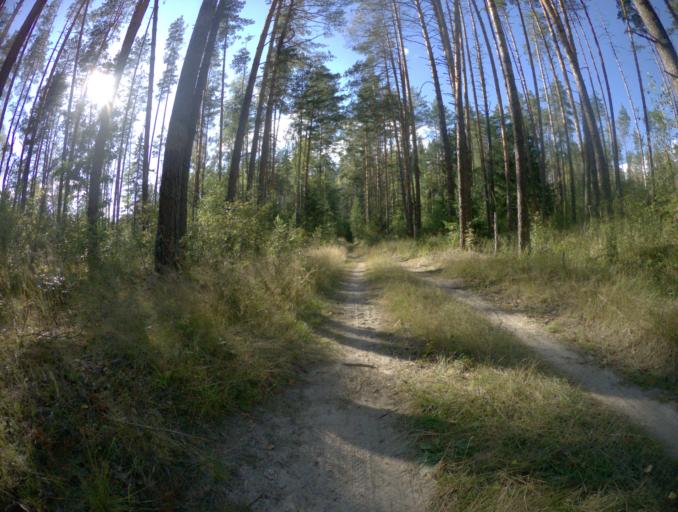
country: RU
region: Vladimir
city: Krasnaya Gorbatka
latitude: 55.8164
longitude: 41.6759
